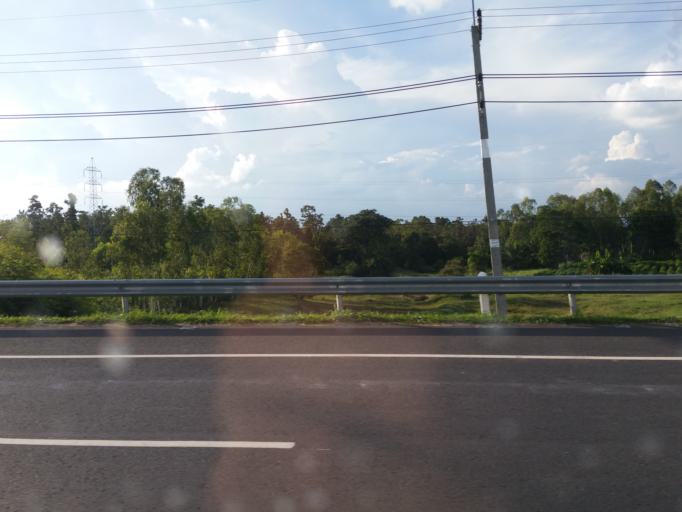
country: TH
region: Changwat Ubon Ratchathani
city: Sirindhorn
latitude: 15.2013
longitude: 105.3718
